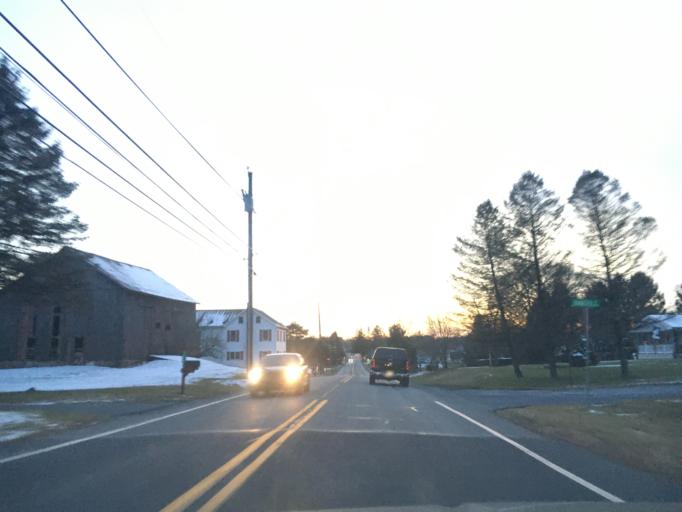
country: US
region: Pennsylvania
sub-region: Northampton County
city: Bath
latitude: 40.7756
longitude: -75.4175
